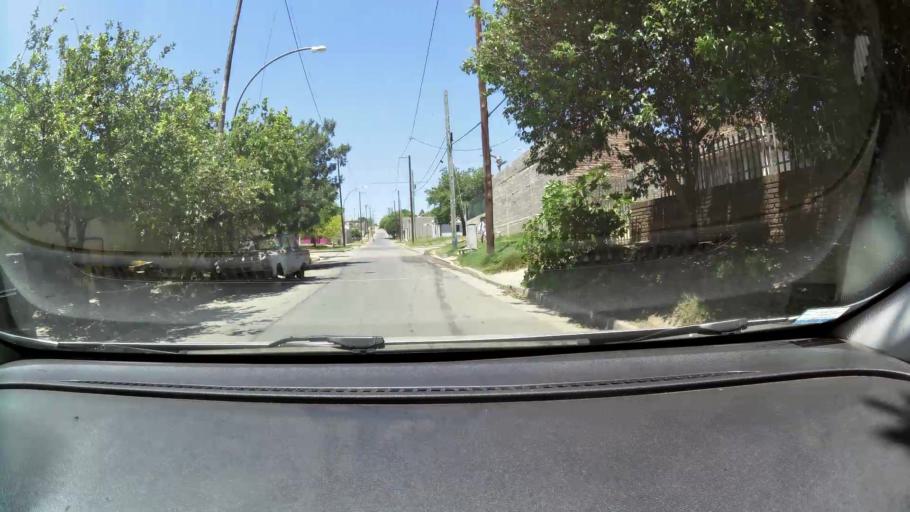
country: AR
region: Cordoba
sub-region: Departamento de Capital
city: Cordoba
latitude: -31.4187
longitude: -64.1193
